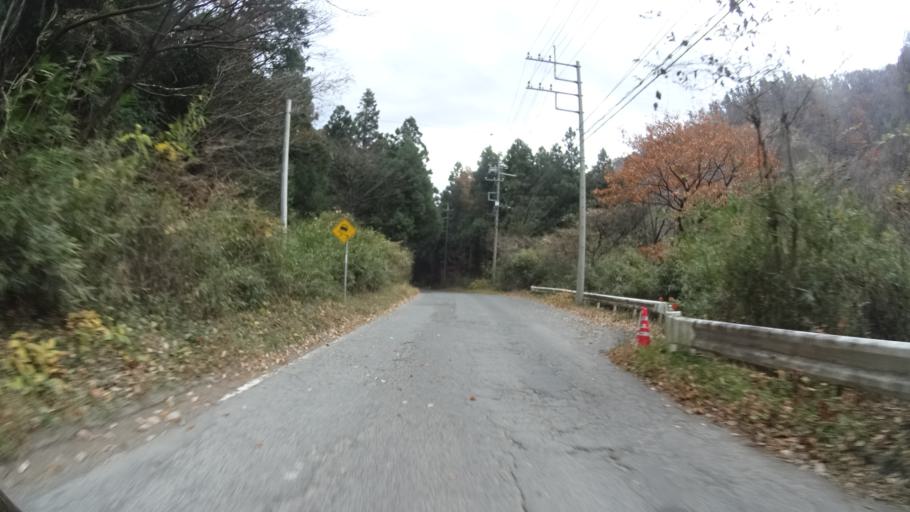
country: JP
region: Gunma
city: Omamacho-omama
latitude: 36.4900
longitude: 139.1854
